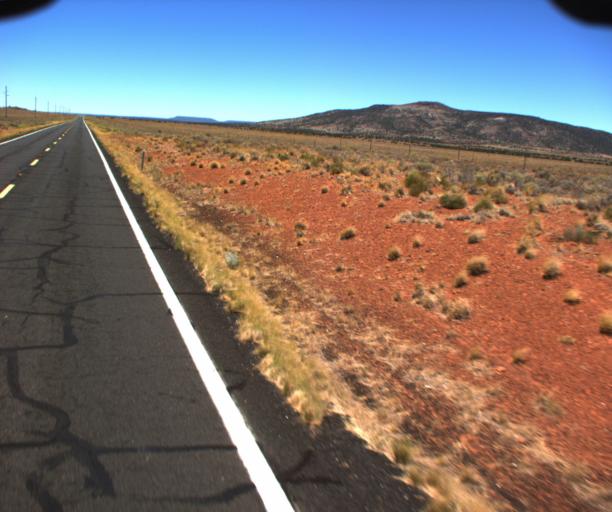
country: US
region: Arizona
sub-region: Coconino County
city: LeChee
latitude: 34.8795
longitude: -110.8870
